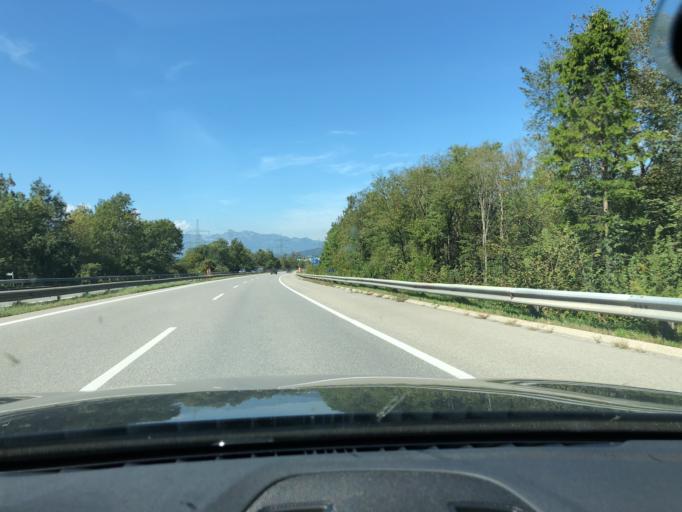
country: AT
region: Vorarlberg
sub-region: Politischer Bezirk Bludenz
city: Bludesch
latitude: 47.1785
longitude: 9.7325
